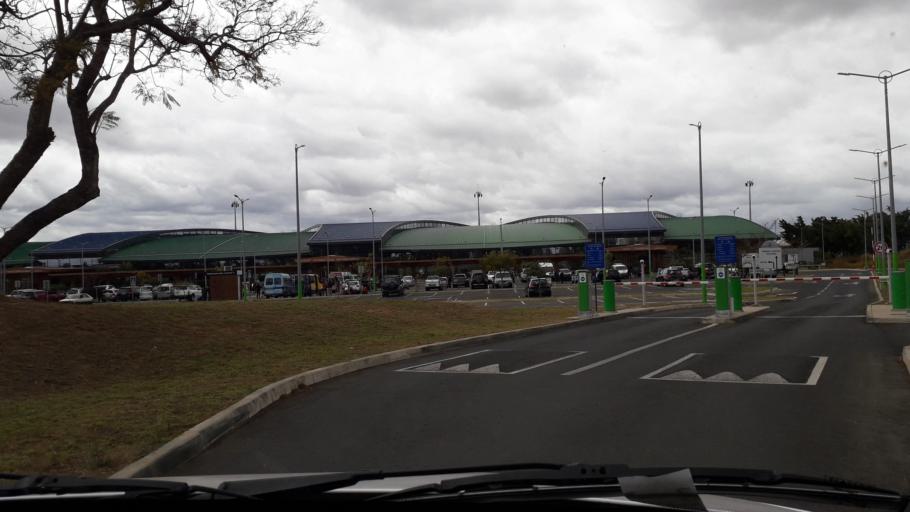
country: MG
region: Analamanga
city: Antananarivo
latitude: -18.8024
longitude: 47.4792
